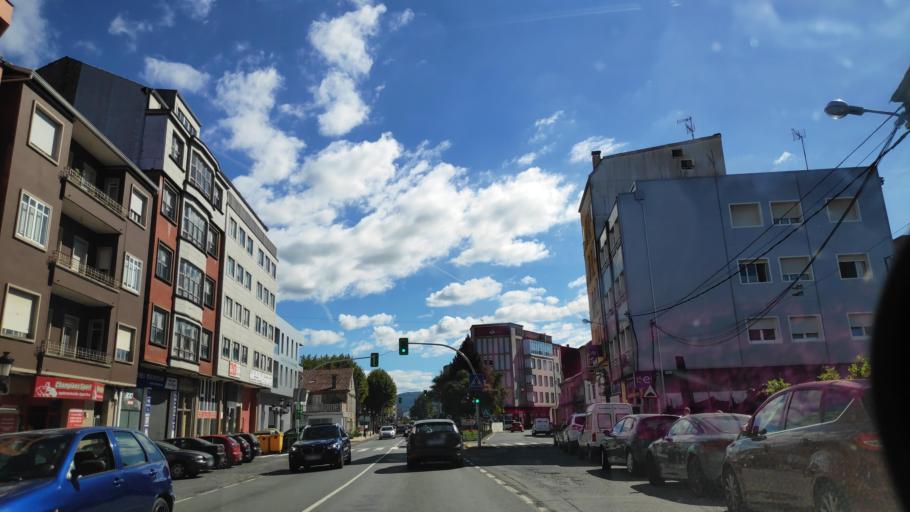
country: ES
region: Galicia
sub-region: Provincia da Coruna
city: Padron
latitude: 42.7402
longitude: -8.6587
